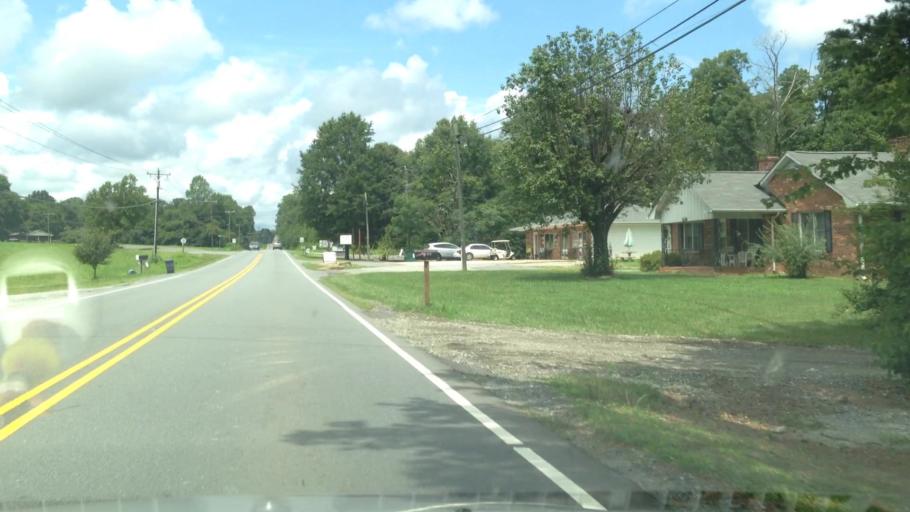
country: US
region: North Carolina
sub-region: Forsyth County
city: Walkertown
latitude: 36.1562
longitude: -80.1298
